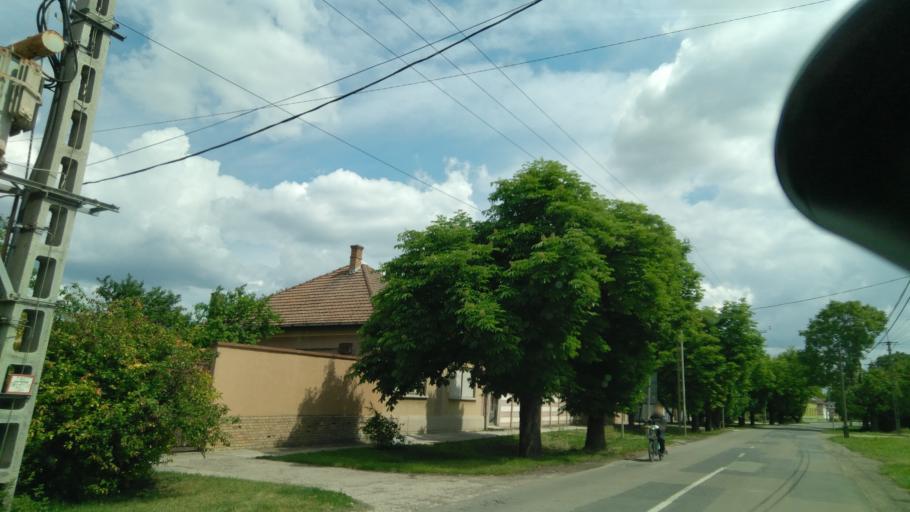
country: HU
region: Bekes
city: Totkomlos
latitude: 46.4127
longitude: 20.7405
